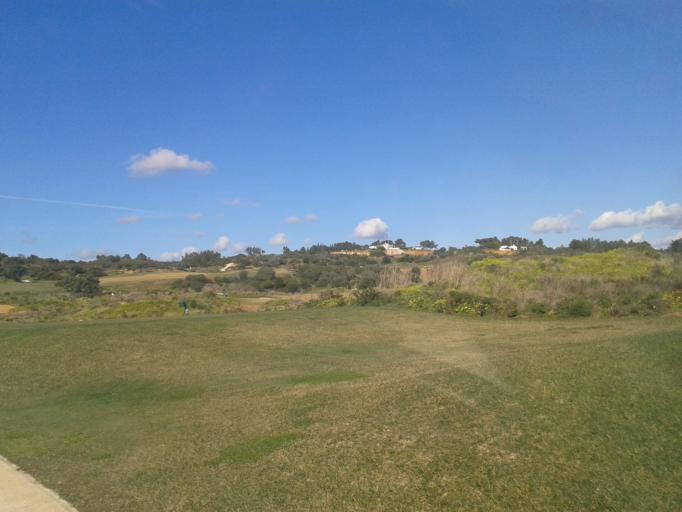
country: PT
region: Faro
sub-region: Lagos
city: Lagos
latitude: 37.1204
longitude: -8.6441
